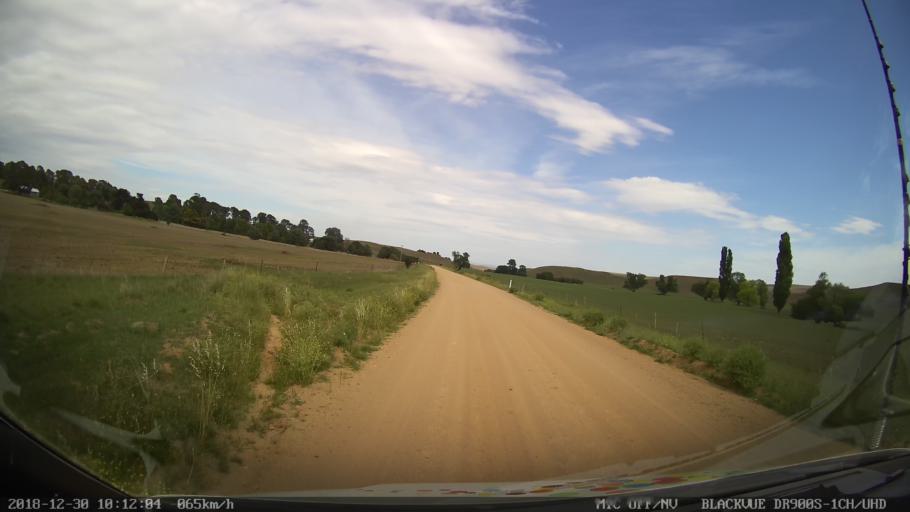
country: AU
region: New South Wales
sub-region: Snowy River
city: Berridale
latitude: -36.5435
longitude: 149.0792
